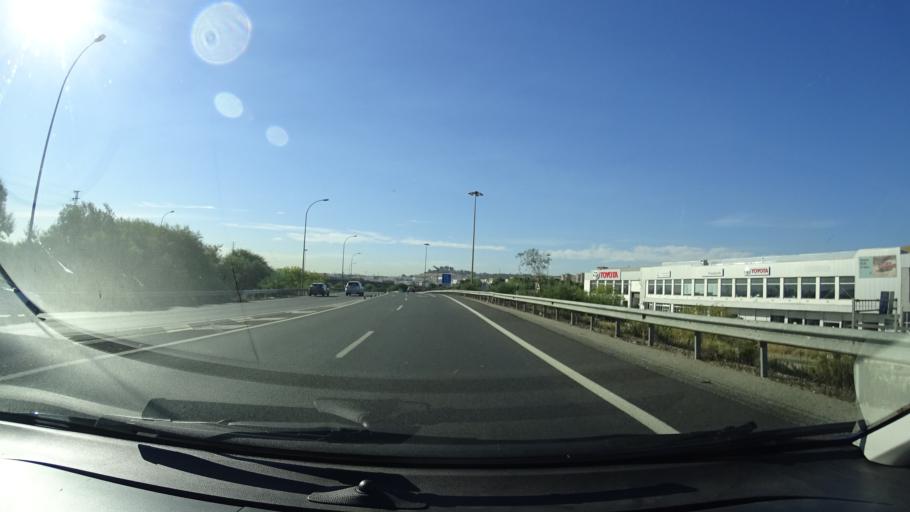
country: ES
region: Andalusia
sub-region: Provincia de Sevilla
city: Camas
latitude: 37.4126
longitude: -6.0342
